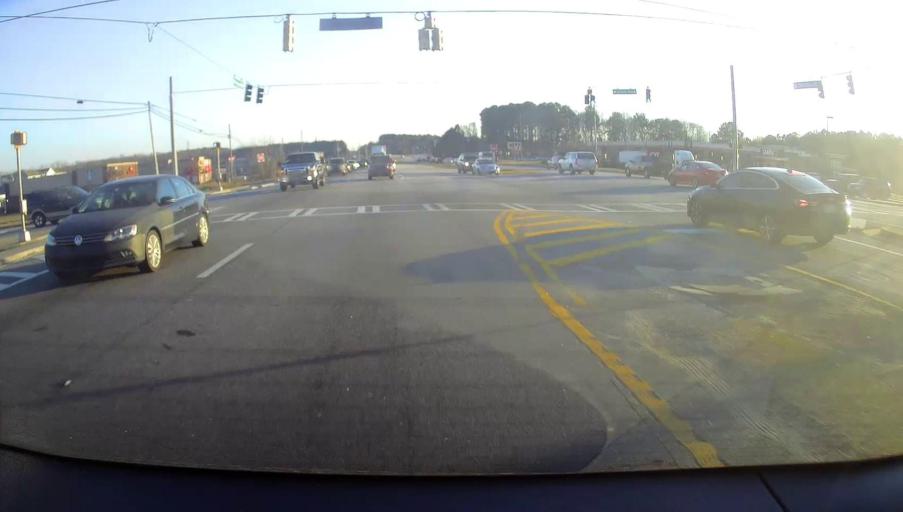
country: US
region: Georgia
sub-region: Fulton County
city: Fairburn
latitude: 33.5396
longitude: -84.5769
